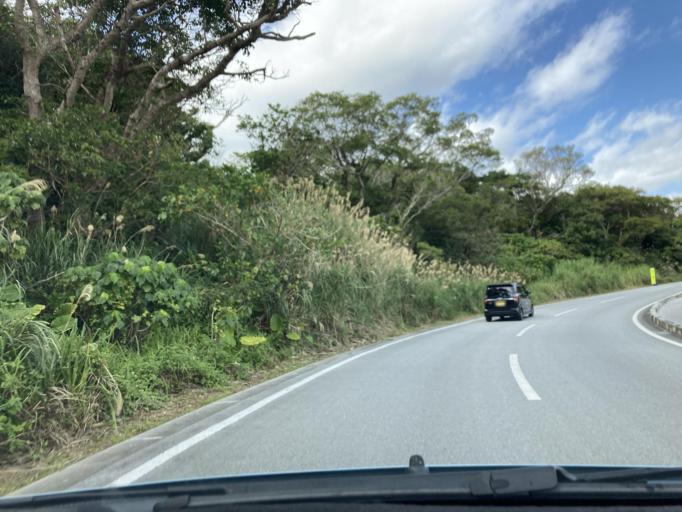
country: JP
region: Okinawa
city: Tomigusuku
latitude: 26.1822
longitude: 127.7591
